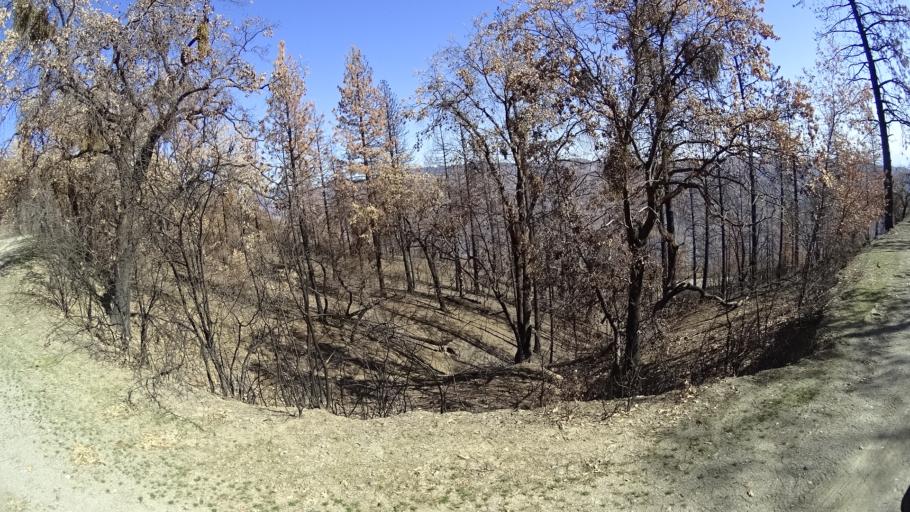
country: US
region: California
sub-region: Tehama County
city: Rancho Tehama Reserve
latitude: 39.6693
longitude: -122.6915
